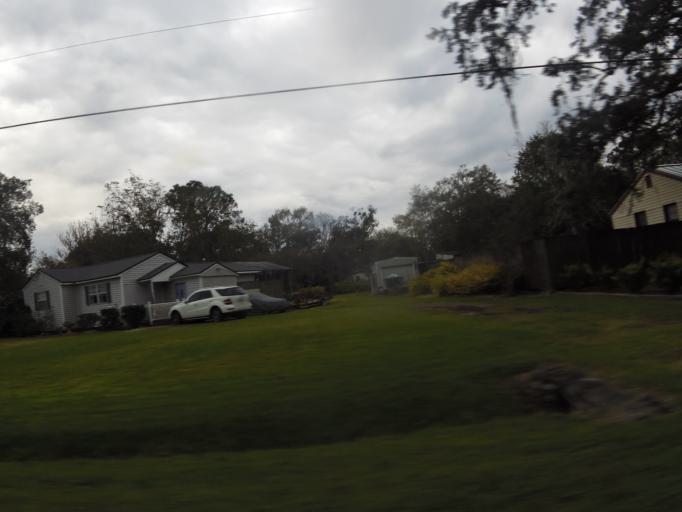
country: US
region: Florida
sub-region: Duval County
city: Jacksonville
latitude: 30.2684
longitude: -81.5956
